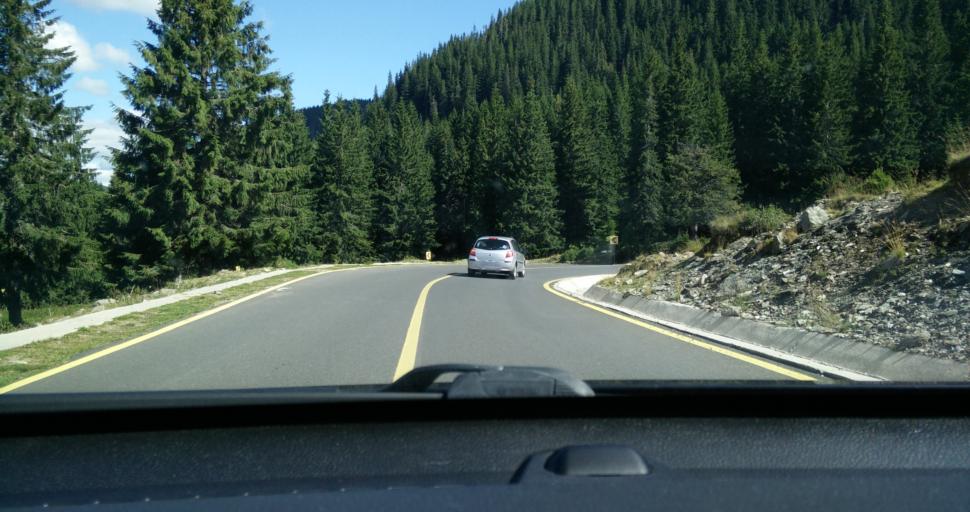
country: RO
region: Gorj
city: Novaci-Straini
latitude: 45.3904
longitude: 23.6398
